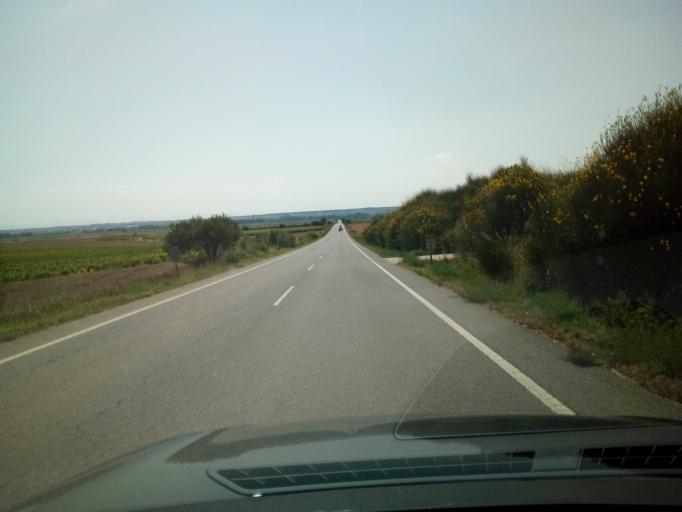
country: ES
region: Navarre
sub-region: Provincia de Navarra
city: Beire
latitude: 42.4930
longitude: -1.6078
